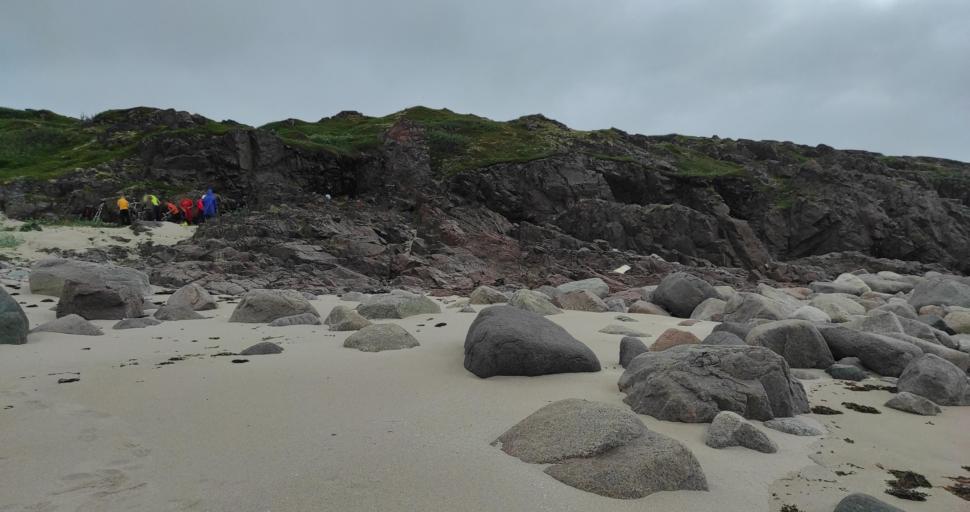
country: RU
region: Murmansk
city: Teriberka
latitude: 69.1997
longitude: 35.5959
